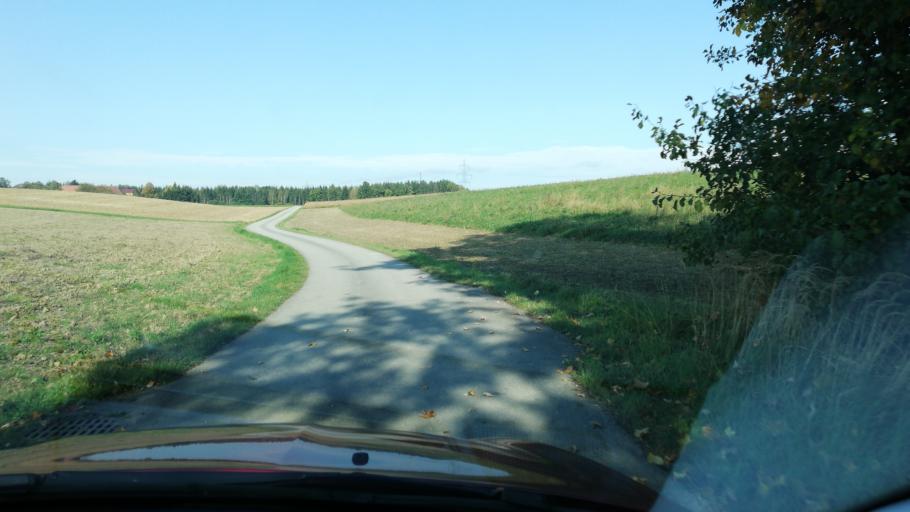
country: AT
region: Upper Austria
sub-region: Politischer Bezirk Kirchdorf an der Krems
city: Kremsmunster
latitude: 48.0964
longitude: 14.1628
